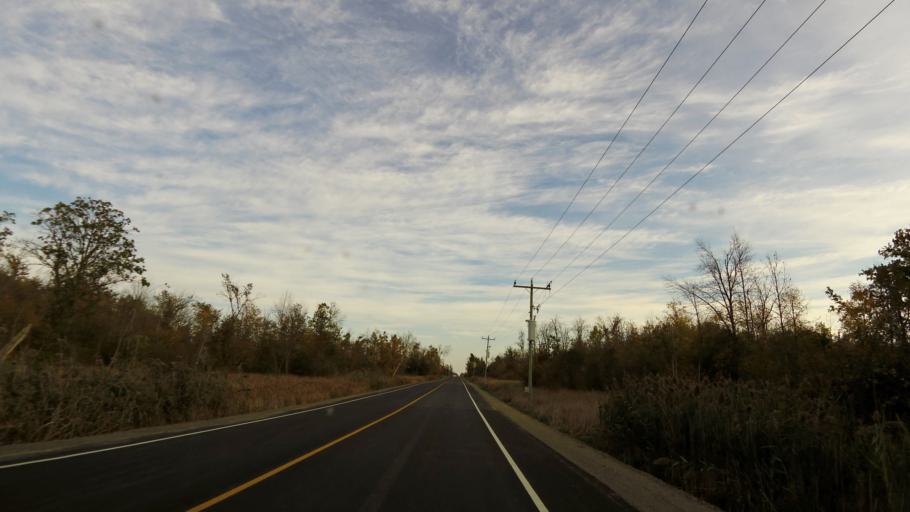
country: CA
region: Ontario
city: Brampton
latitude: 43.6987
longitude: -79.9210
